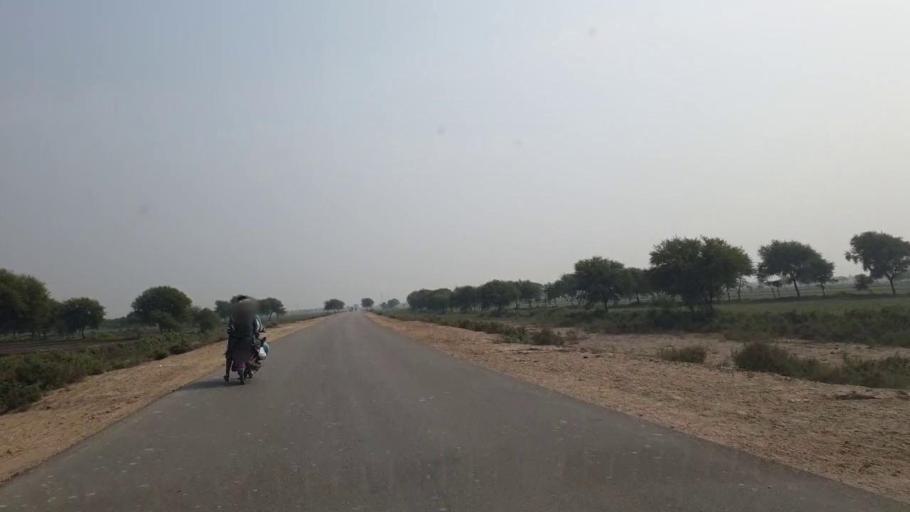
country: PK
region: Sindh
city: Matli
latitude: 25.0616
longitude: 68.6660
